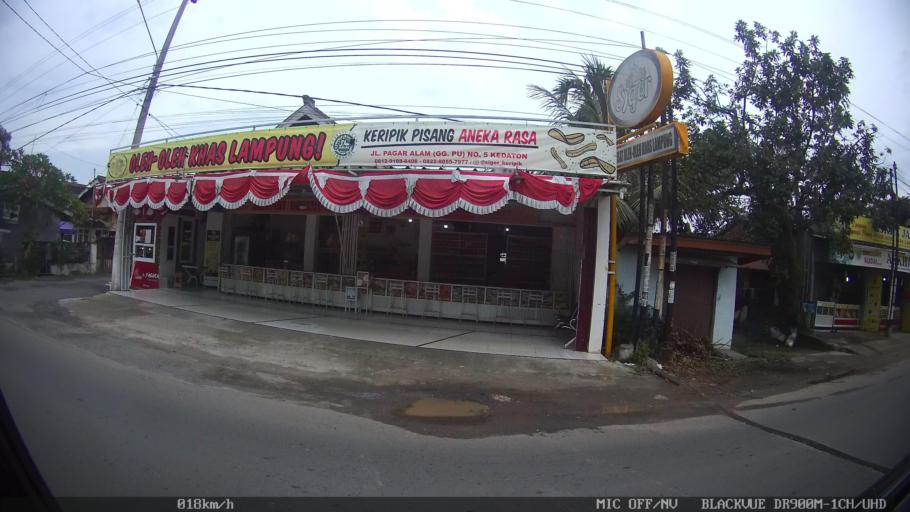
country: ID
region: Lampung
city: Kedaton
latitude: -5.3839
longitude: 105.2590
